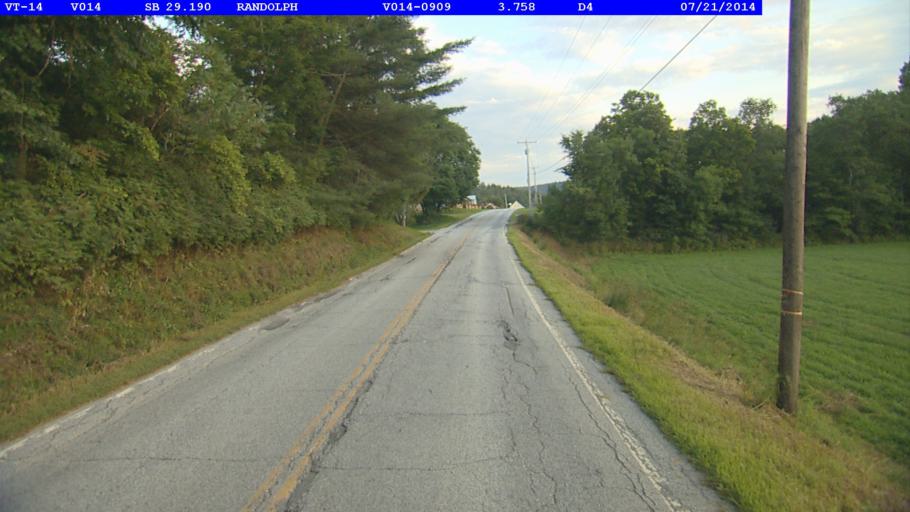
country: US
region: Vermont
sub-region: Orange County
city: Randolph
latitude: 43.9235
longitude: -72.5537
